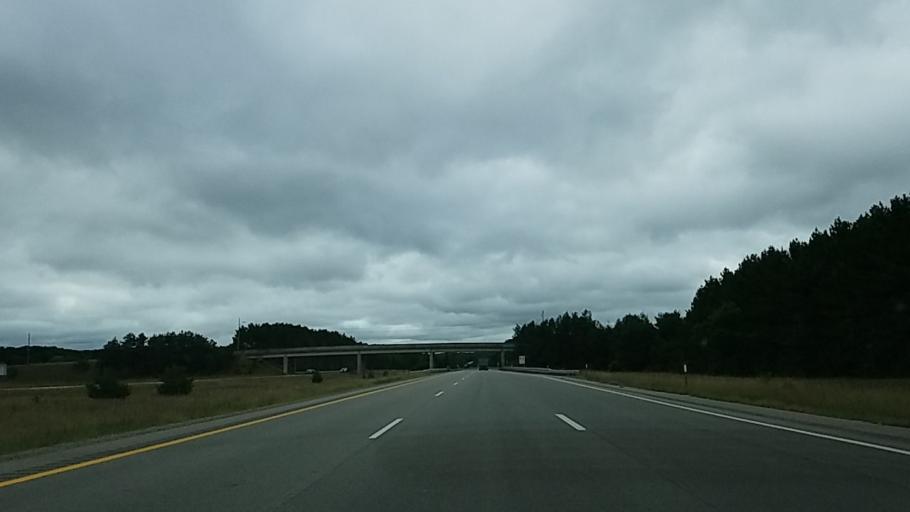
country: US
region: Michigan
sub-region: Otsego County
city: Gaylord
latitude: 45.1446
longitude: -84.6706
